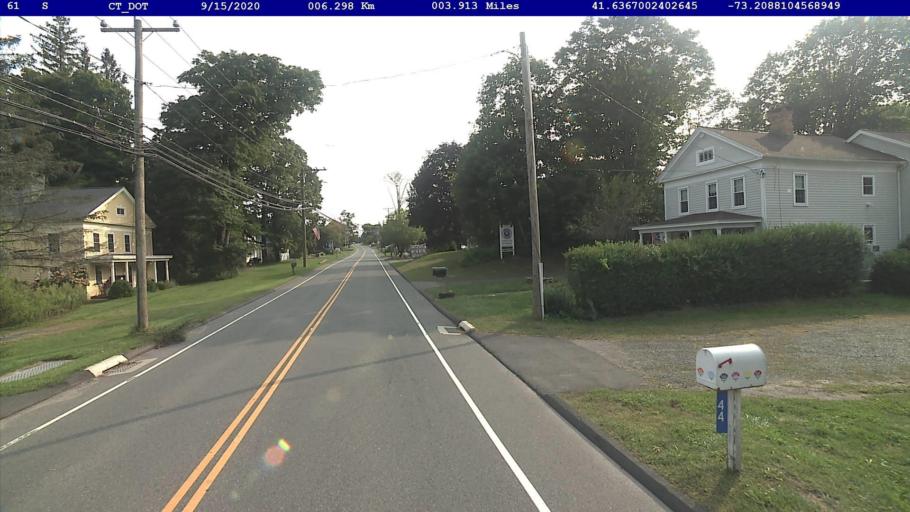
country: US
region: Connecticut
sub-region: Litchfield County
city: Bethlehem Village
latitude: 41.6367
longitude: -73.2088
